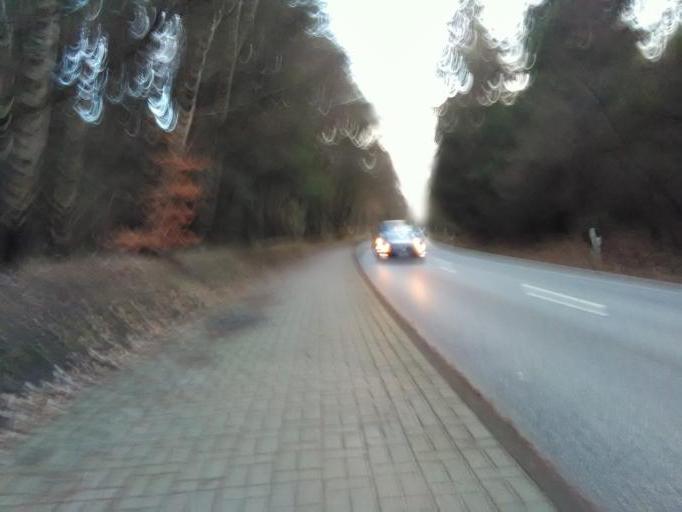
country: DE
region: Schleswig-Holstein
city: Norderstedt
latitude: 53.7198
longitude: 9.9760
